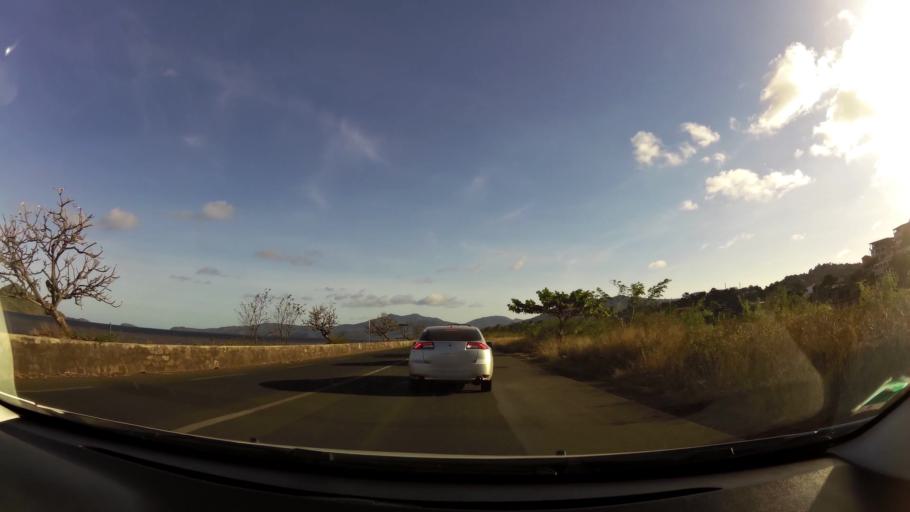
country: YT
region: Mamoudzou
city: Mamoudzou
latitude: -12.7884
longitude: 45.2249
